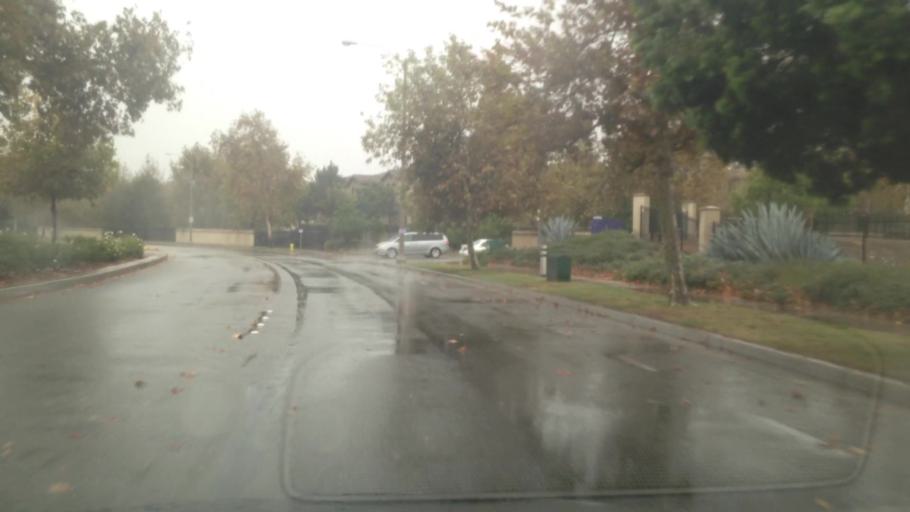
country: US
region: California
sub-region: Riverside County
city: Home Gardens
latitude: 33.9088
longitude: -117.4954
